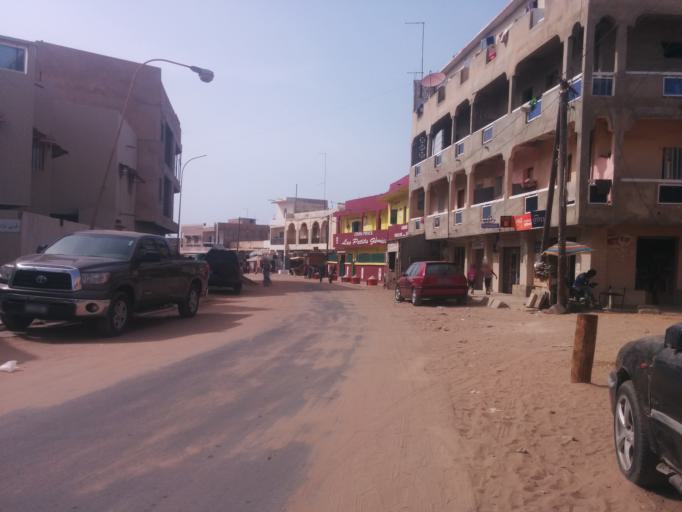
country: SN
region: Dakar
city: Pikine
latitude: 14.7643
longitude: -17.4377
